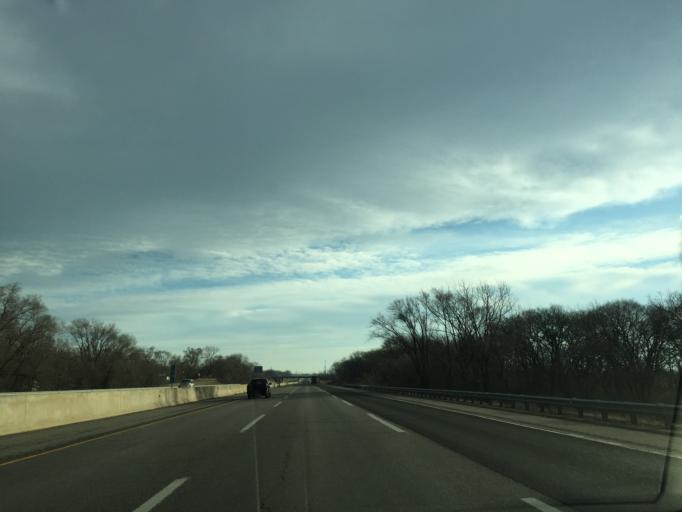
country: US
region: Indiana
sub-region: Lake County
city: New Chicago
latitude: 41.5891
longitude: -87.2757
